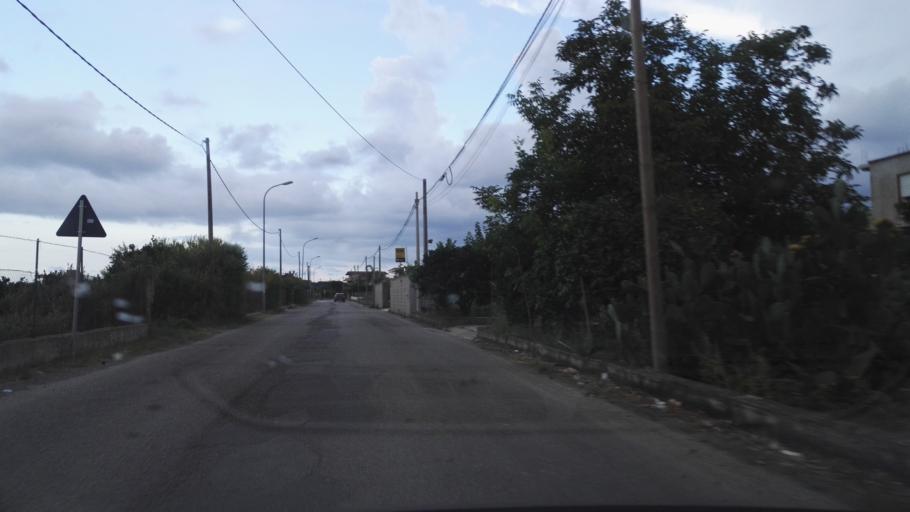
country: IT
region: Calabria
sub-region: Provincia di Reggio Calabria
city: Caulonia Marina
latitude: 38.3545
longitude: 16.4702
